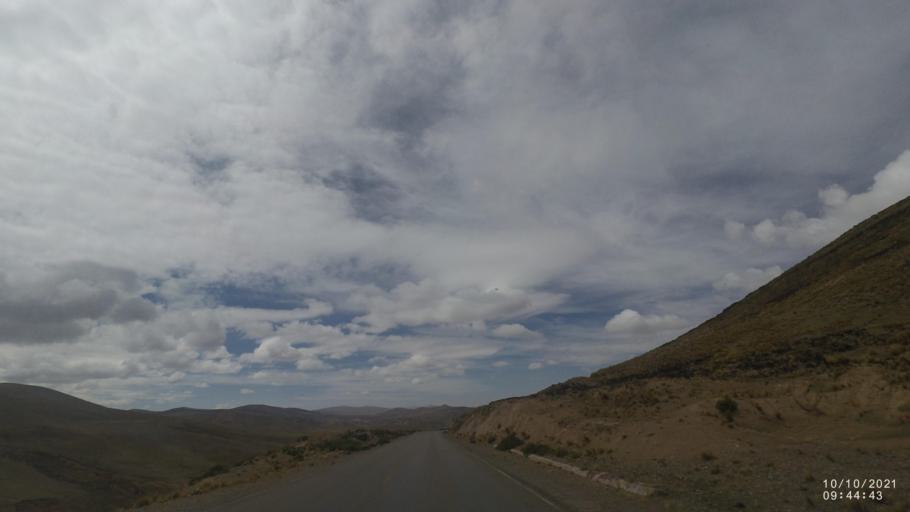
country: BO
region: La Paz
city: Quime
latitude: -17.1625
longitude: -67.3349
